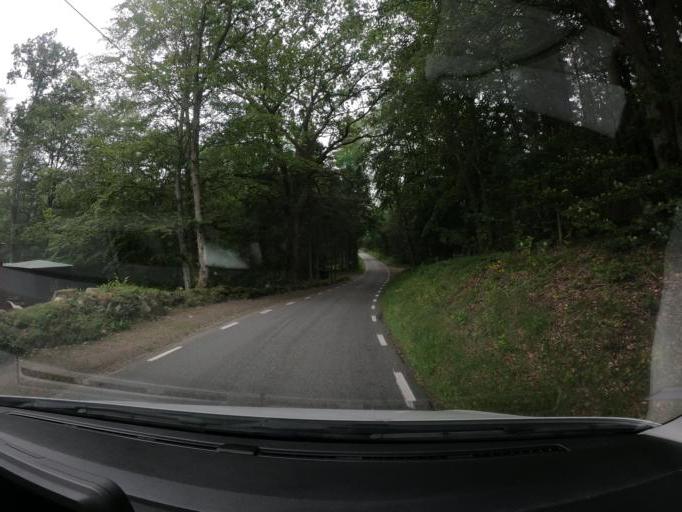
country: SE
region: Skane
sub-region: Hoors Kommun
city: Hoeoer
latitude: 56.0169
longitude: 13.5568
